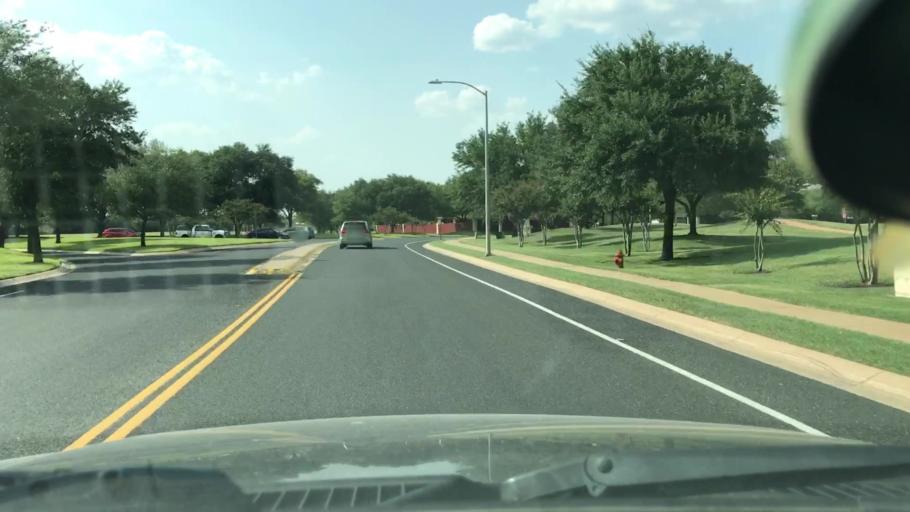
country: US
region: Texas
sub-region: Williamson County
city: Leander
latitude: 30.5444
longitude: -97.8354
